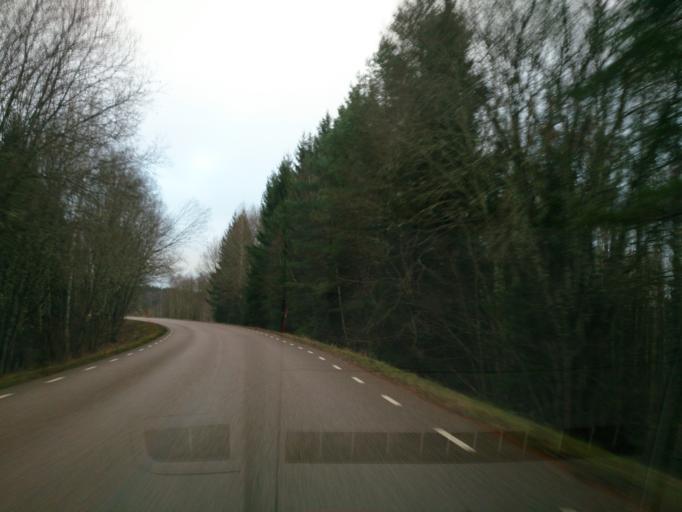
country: SE
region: OEstergoetland
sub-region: Atvidabergs Kommun
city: Atvidaberg
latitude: 58.2349
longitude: 16.0086
